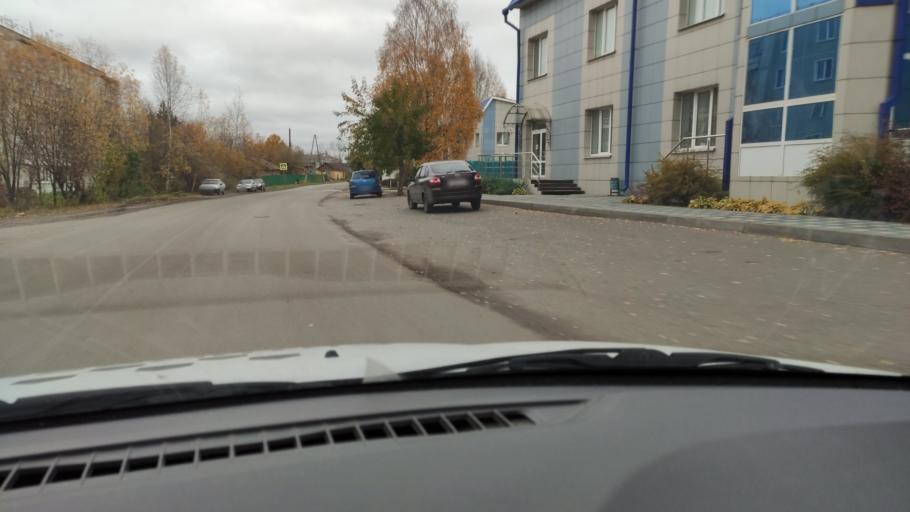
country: RU
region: Kirov
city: Slobodskoy
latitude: 58.7204
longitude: 50.1749
